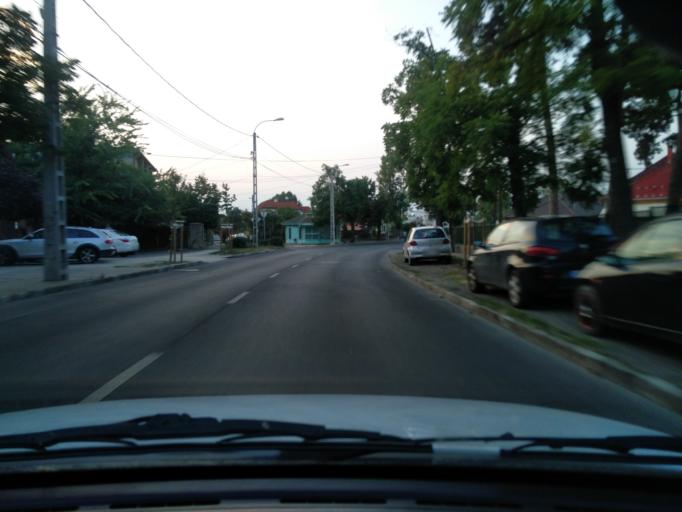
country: HU
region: Budapest
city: Budapest XXIII. keruelet
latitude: 47.4050
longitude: 19.0909
